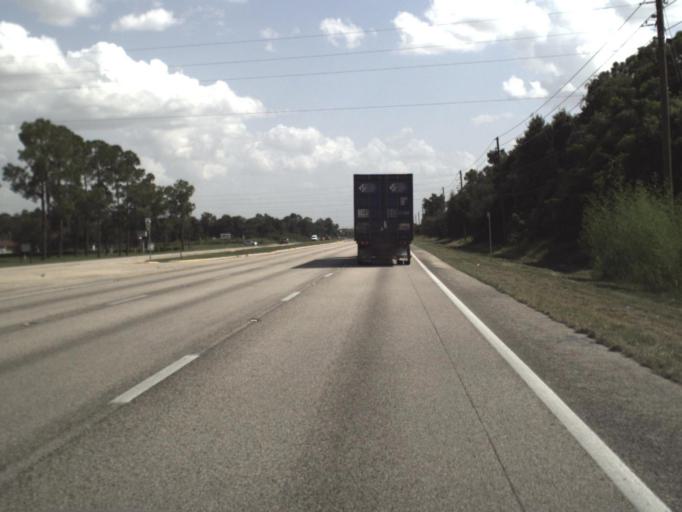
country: US
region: Florida
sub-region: Polk County
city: Lake Wales
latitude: 27.9412
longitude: -81.6137
